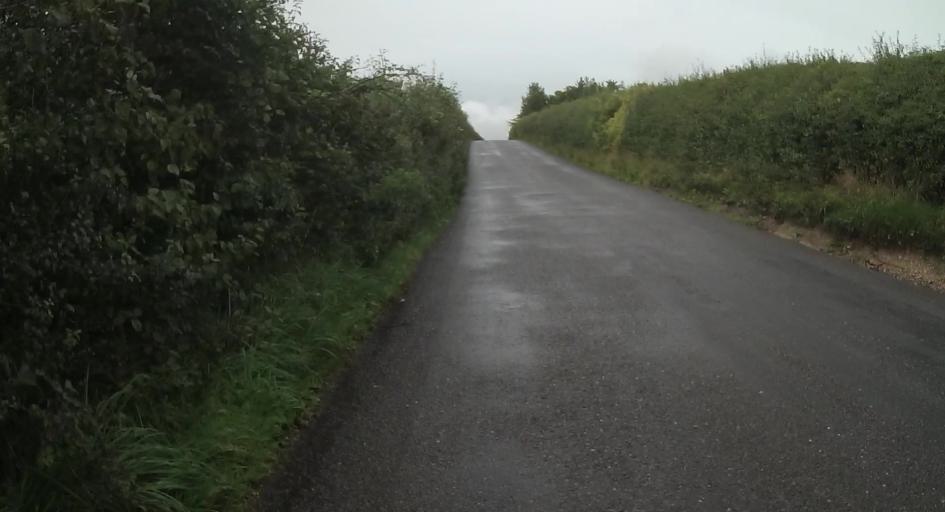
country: GB
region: England
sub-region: Hampshire
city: Tadley
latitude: 51.2932
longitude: -1.1493
